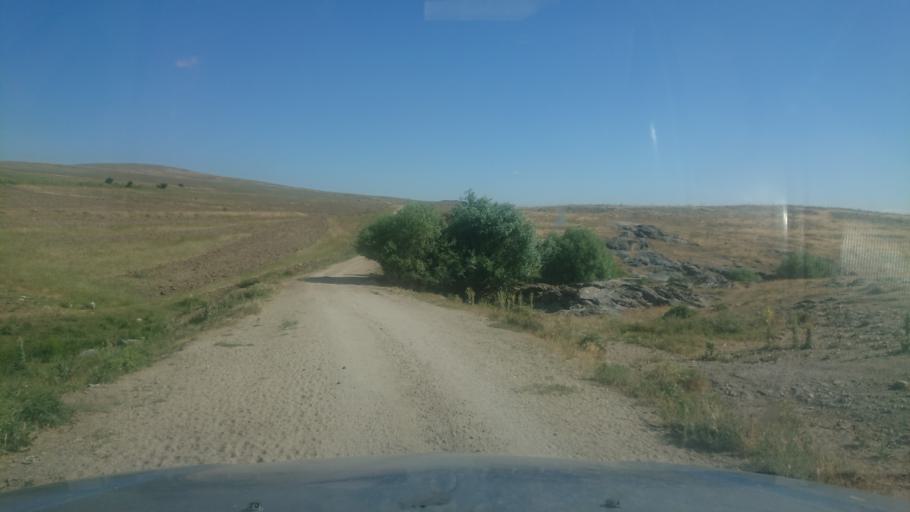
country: TR
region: Aksaray
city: Sariyahsi
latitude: 38.9130
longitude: 33.8553
